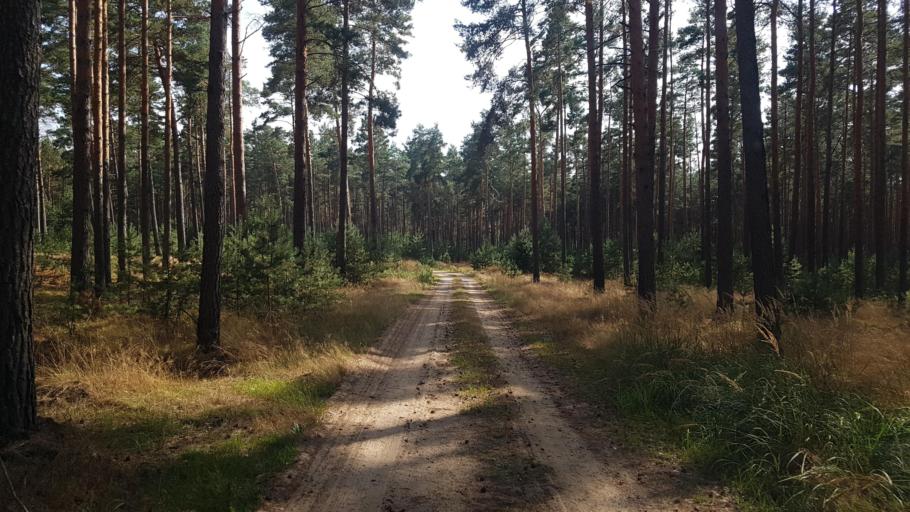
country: DE
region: Brandenburg
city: Dahme
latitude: 51.9636
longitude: 13.4185
